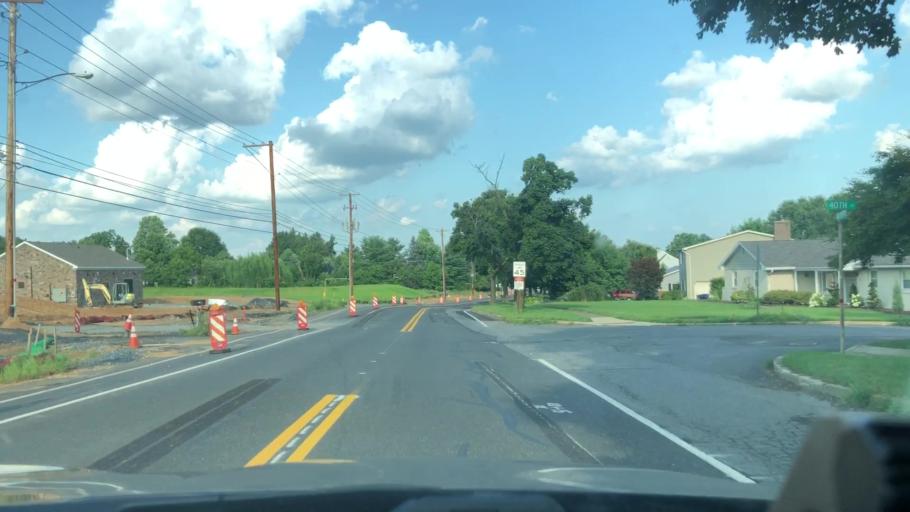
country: US
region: Pennsylvania
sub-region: Lehigh County
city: Wescosville
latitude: 40.6137
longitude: -75.5511
